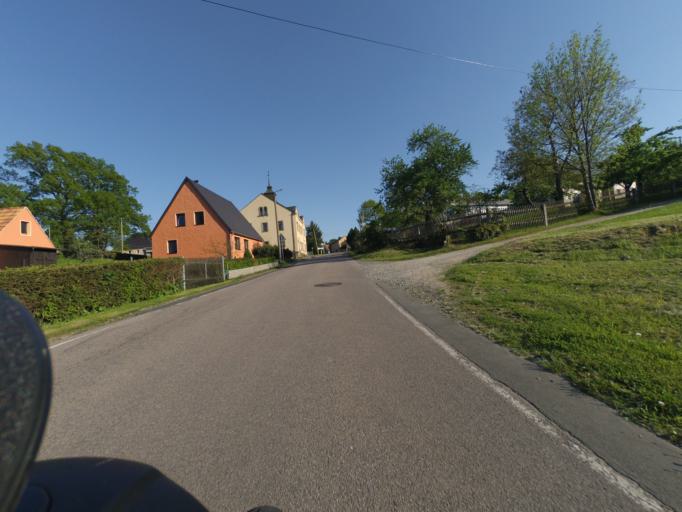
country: DE
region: Saxony
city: Obercunnersdorf
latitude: 50.8874
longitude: 13.5836
